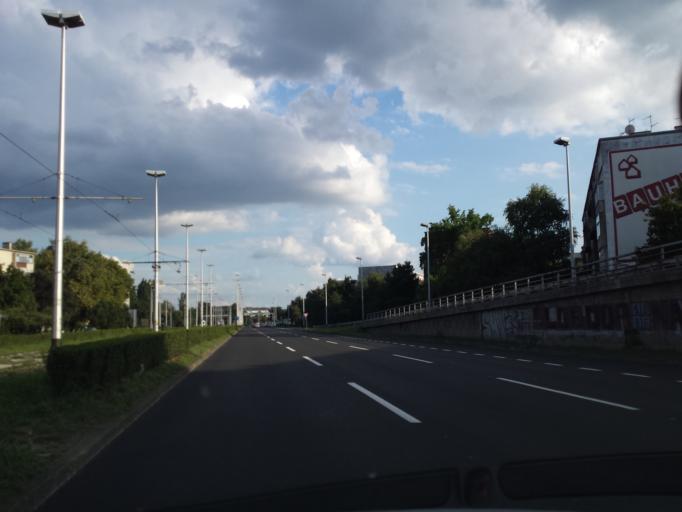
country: HR
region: Grad Zagreb
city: Novi Zagreb
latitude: 45.7941
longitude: 16.0007
